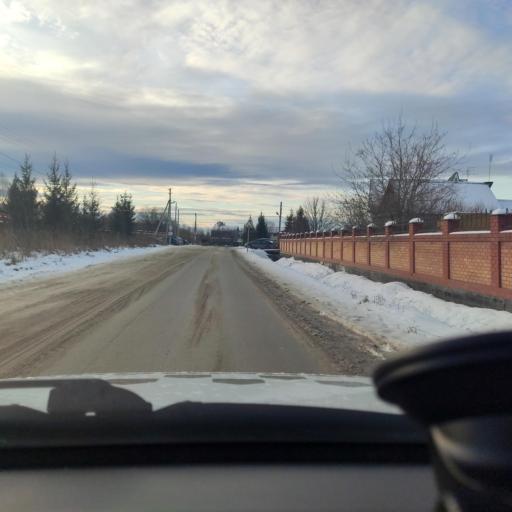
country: RU
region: Perm
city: Ferma
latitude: 57.9458
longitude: 56.3588
